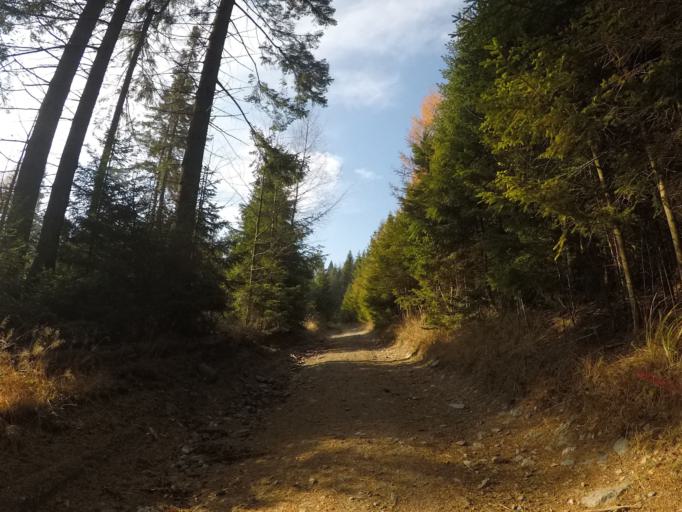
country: SK
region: Kosicky
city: Gelnica
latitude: 48.7594
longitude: 21.0477
